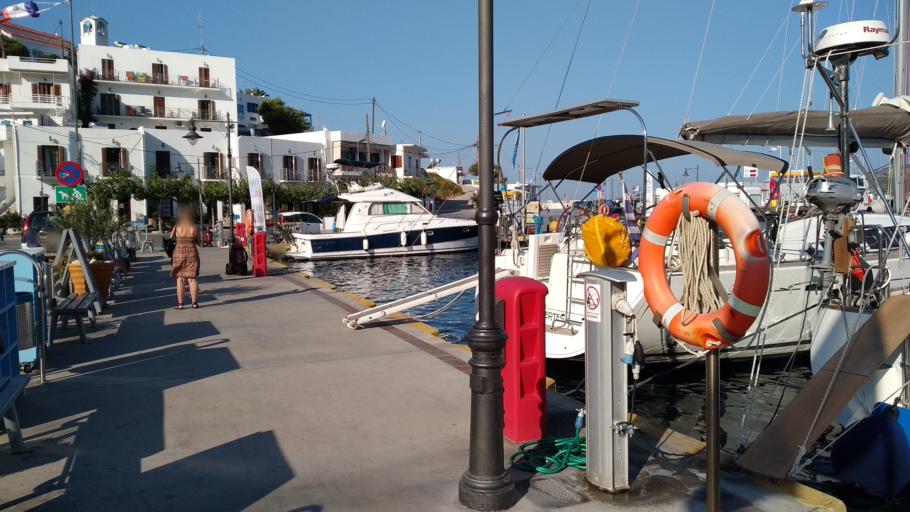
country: GR
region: Central Greece
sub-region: Nomos Evvoias
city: Skyros
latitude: 38.8422
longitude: 24.5376
